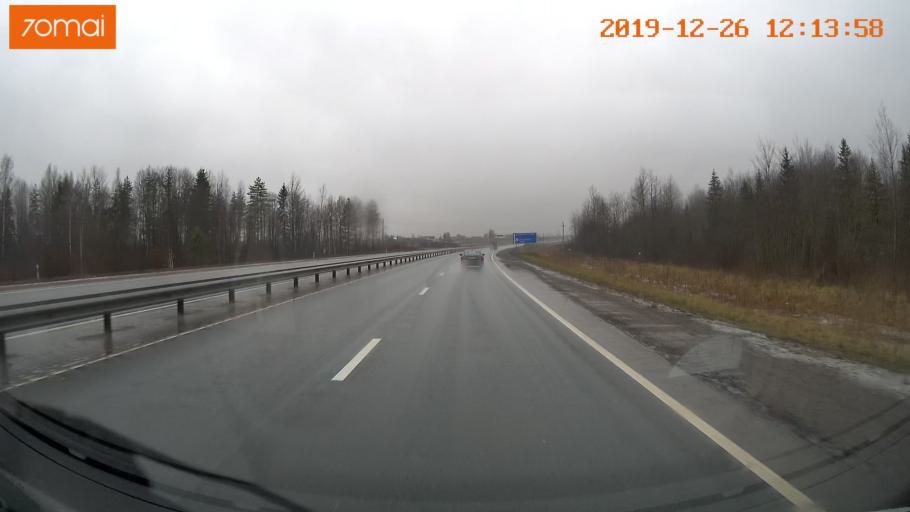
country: RU
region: Vologda
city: Tonshalovo
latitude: 59.2155
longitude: 37.9480
